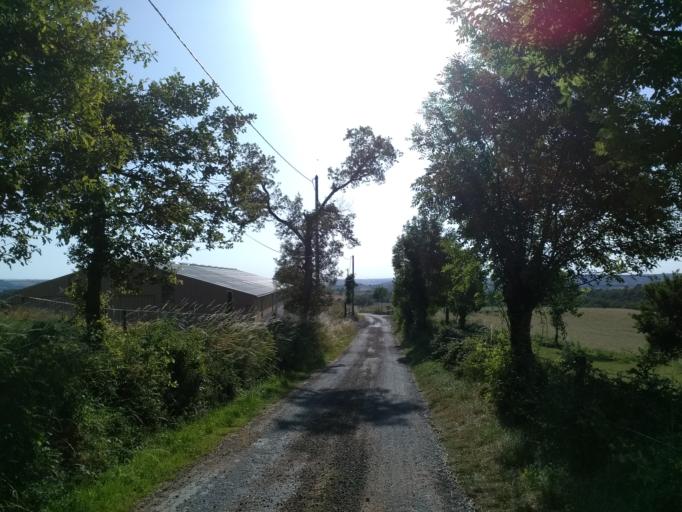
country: FR
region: Midi-Pyrenees
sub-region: Departement de l'Aveyron
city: La Loubiere
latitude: 44.3664
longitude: 2.6964
